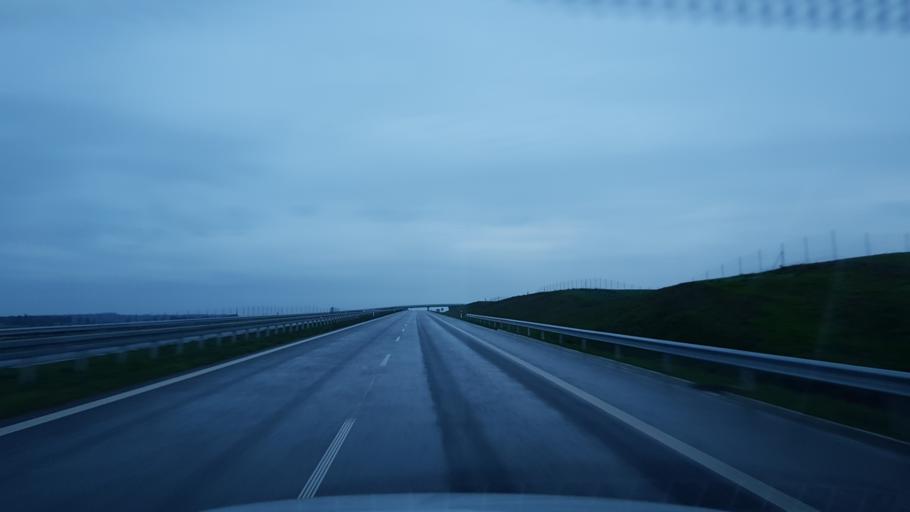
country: PL
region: West Pomeranian Voivodeship
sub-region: Powiat gryficki
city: Brojce
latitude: 53.9730
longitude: 15.4269
